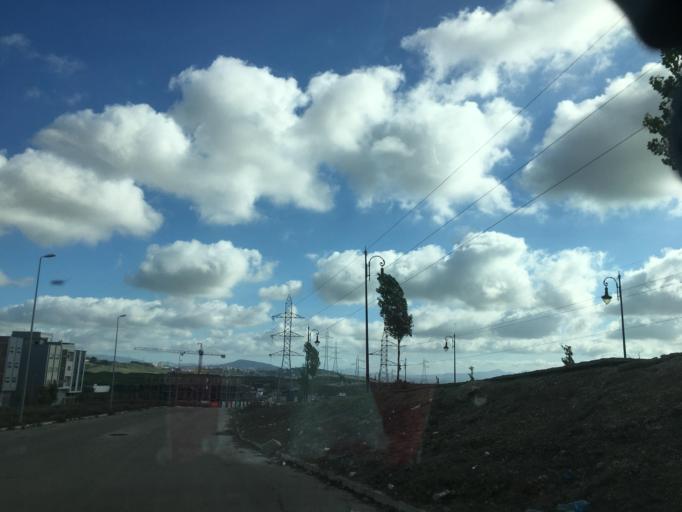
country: MA
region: Tanger-Tetouan
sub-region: Tanger-Assilah
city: Tangier
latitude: 35.7088
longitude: -5.8176
